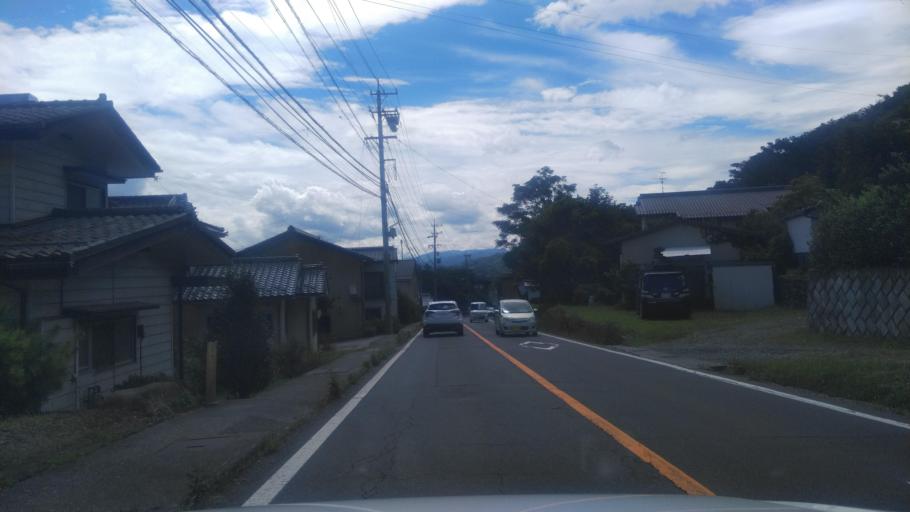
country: JP
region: Nagano
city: Ueda
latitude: 36.4130
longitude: 138.2900
